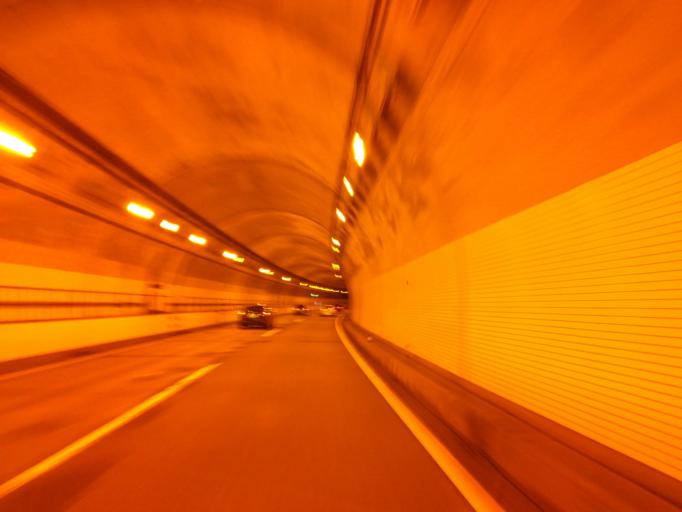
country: JP
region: Nagano
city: Saku
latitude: 36.2974
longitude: 138.6725
